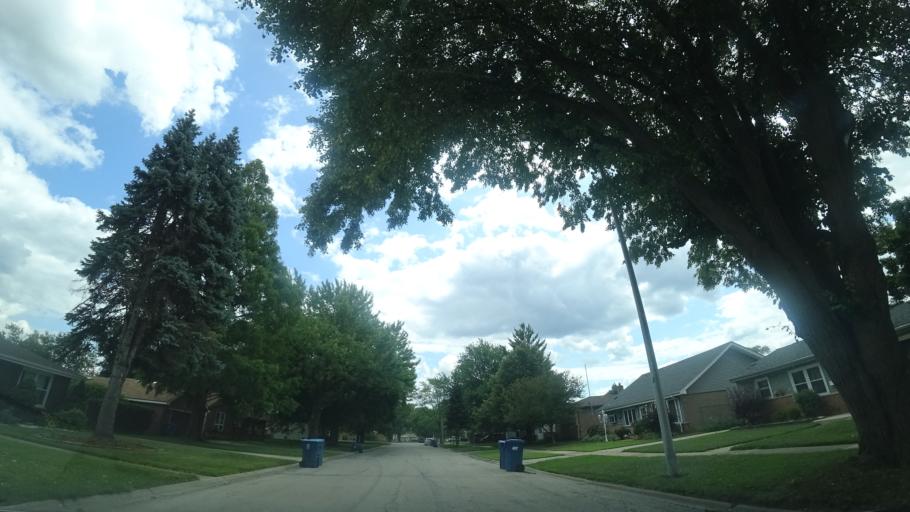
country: US
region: Illinois
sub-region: Cook County
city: Alsip
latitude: 41.6812
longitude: -87.7260
